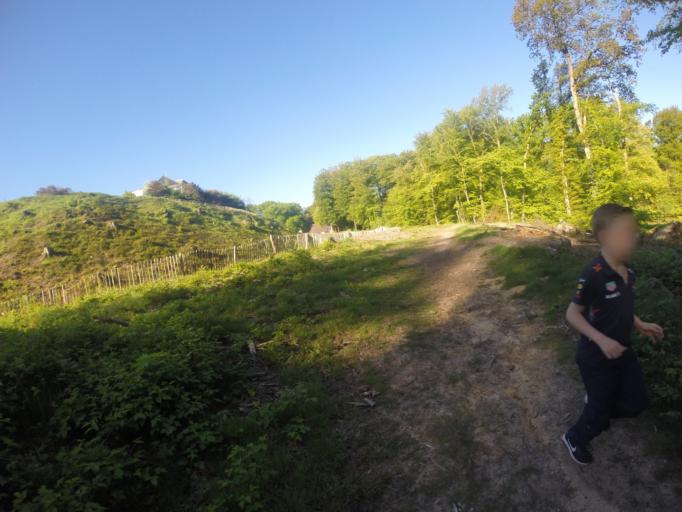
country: NL
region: Gelderland
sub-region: Gemeente Montferland
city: s-Heerenberg
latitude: 51.8966
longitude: 6.2425
